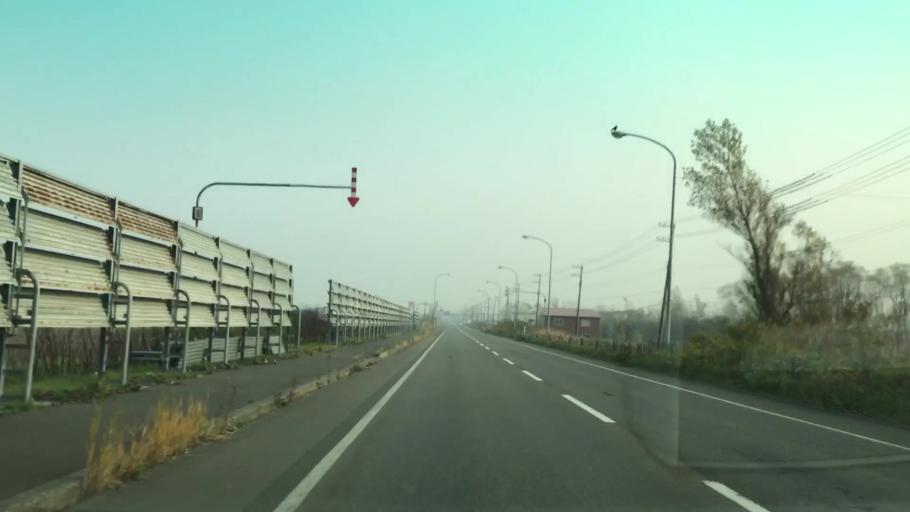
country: JP
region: Hokkaido
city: Ishikari
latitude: 43.2395
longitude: 141.3654
